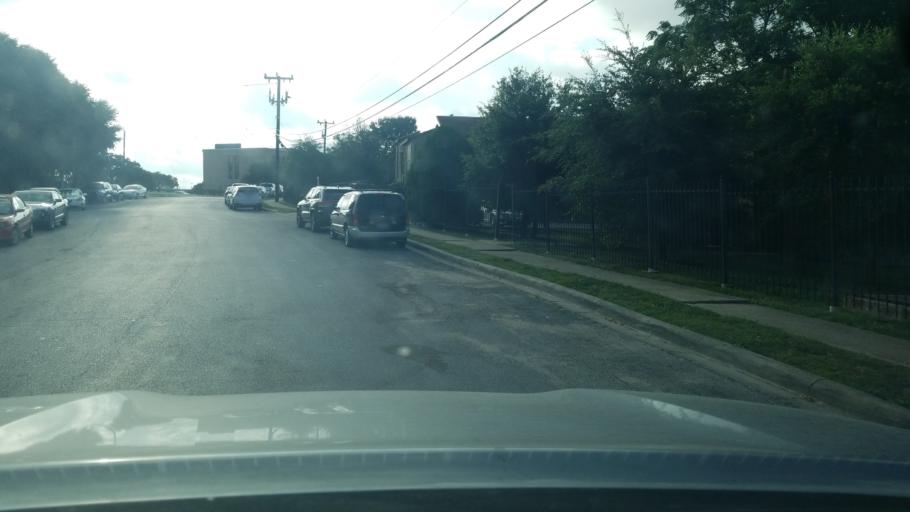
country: US
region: Texas
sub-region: Bexar County
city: Castle Hills
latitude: 29.5332
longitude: -98.4913
